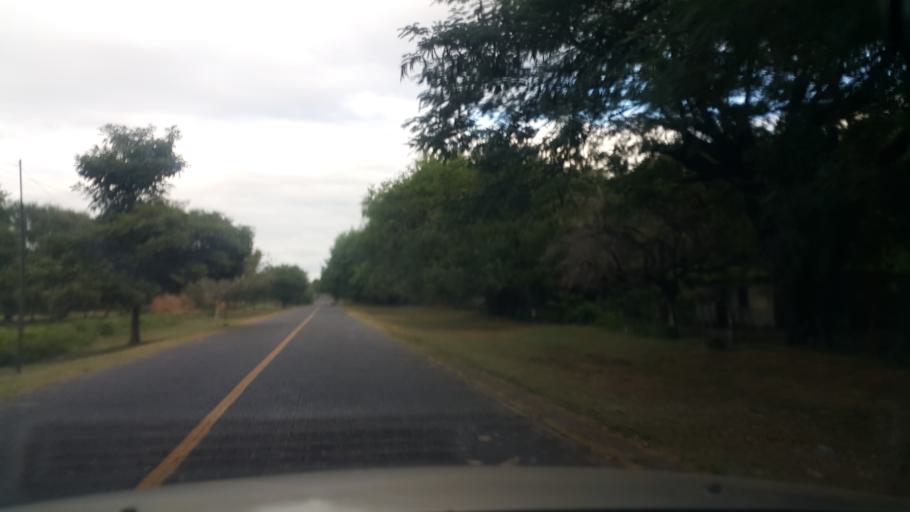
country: NI
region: Rivas
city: Moyogalpa
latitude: 11.5260
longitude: -85.7020
